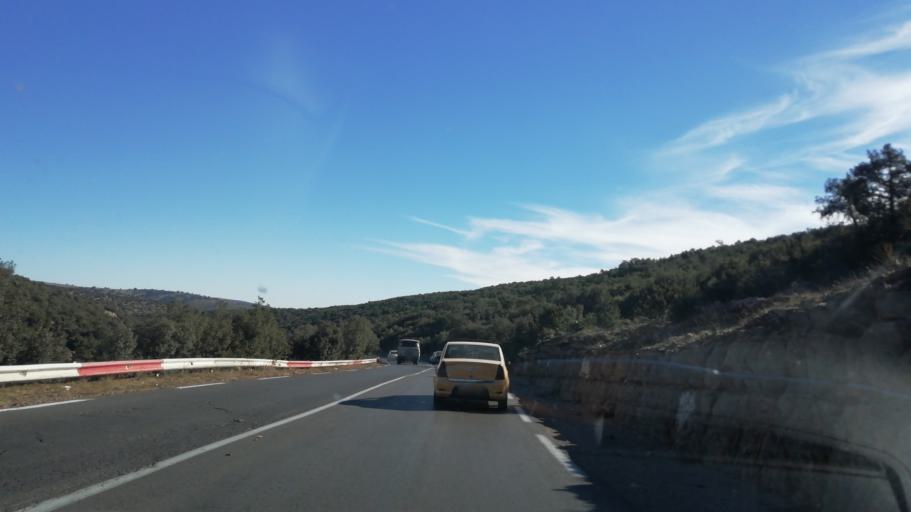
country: DZ
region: Tlemcen
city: Sebdou
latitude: 34.7433
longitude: -1.3489
